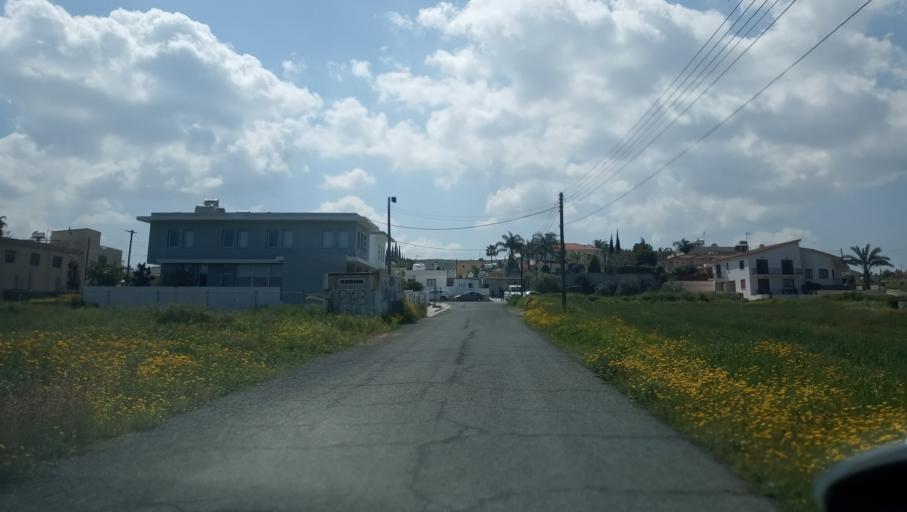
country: CY
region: Lefkosia
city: Dali
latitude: 35.0130
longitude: 33.4001
